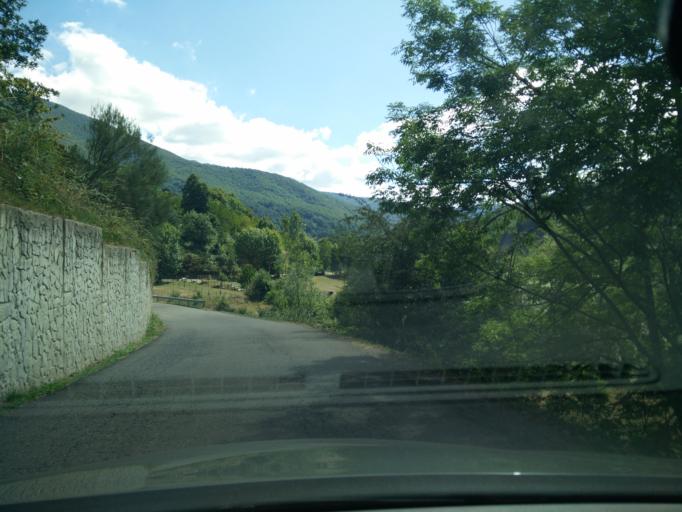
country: ES
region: Castille and Leon
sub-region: Provincia de Leon
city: Posada de Valdeon
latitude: 43.1574
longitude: -4.9131
